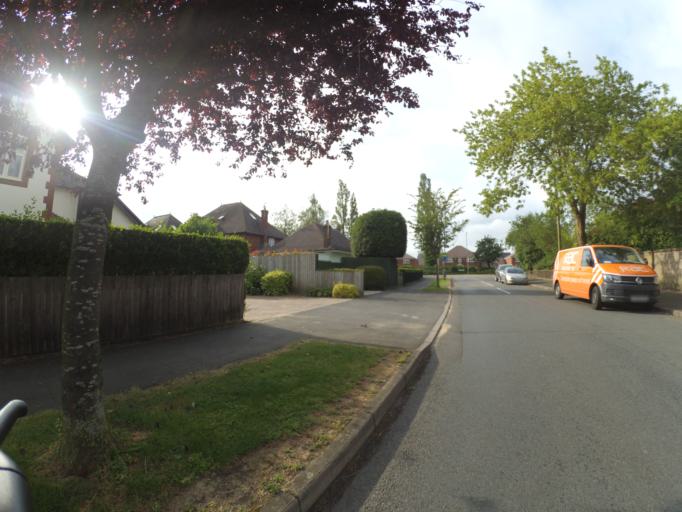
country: GB
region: England
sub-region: Warwickshire
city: Rugby
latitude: 52.3575
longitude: -1.2355
